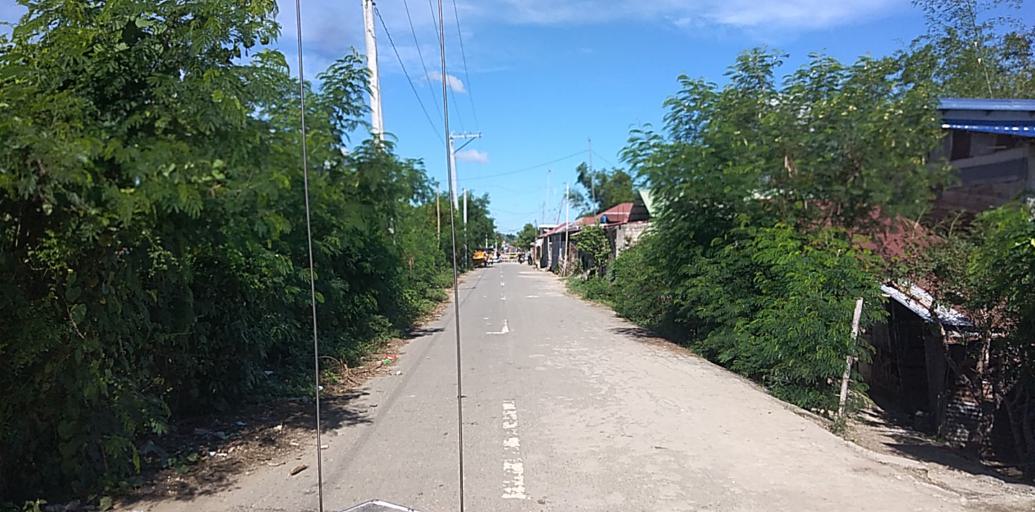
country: PH
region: Central Luzon
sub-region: Province of Pampanga
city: Candating
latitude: 15.1315
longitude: 120.8078
